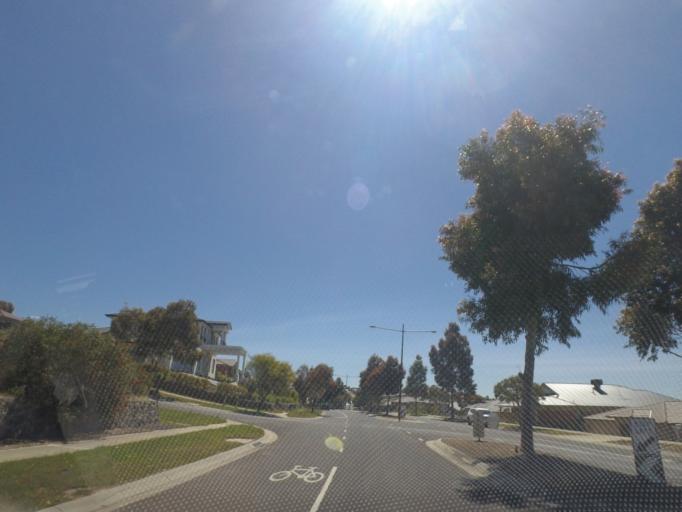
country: AU
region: Victoria
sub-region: Hume
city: Sunbury
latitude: -37.5663
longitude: 144.6977
